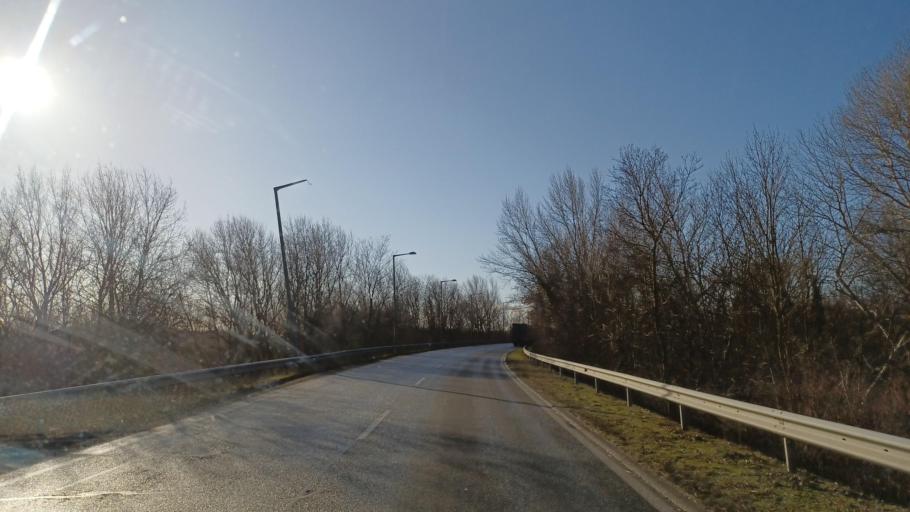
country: HU
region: Tolna
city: Dunafoldvar
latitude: 46.7947
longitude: 18.9266
